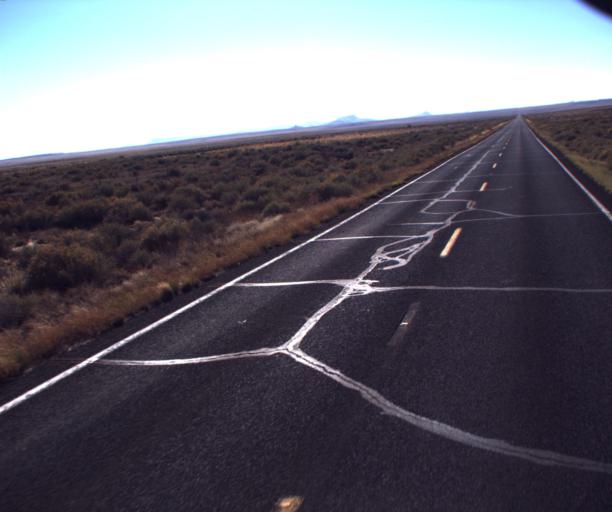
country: US
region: Arizona
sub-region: Navajo County
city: First Mesa
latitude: 35.7164
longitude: -110.5134
